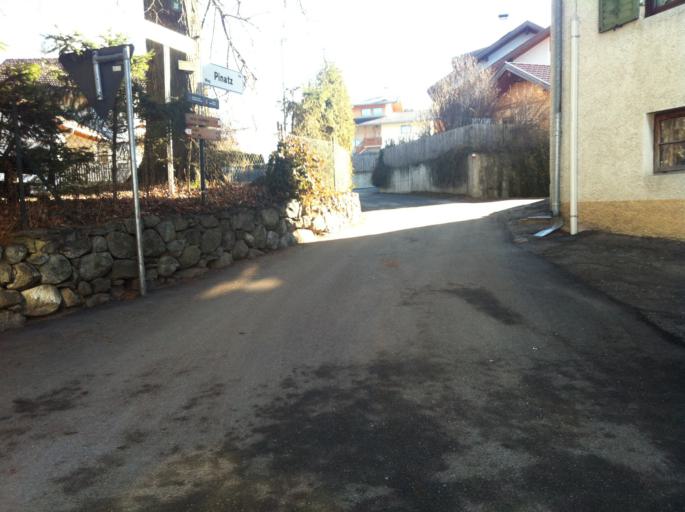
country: IT
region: Trentino-Alto Adige
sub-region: Bolzano
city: Leone-Santa Elisabetta
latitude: 46.7322
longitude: 11.6675
